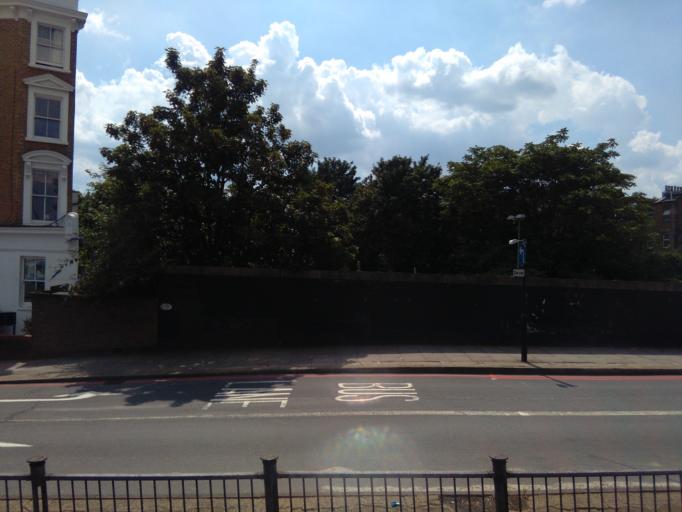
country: GB
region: England
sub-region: Greater London
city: Catford
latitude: 51.4758
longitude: -0.0321
